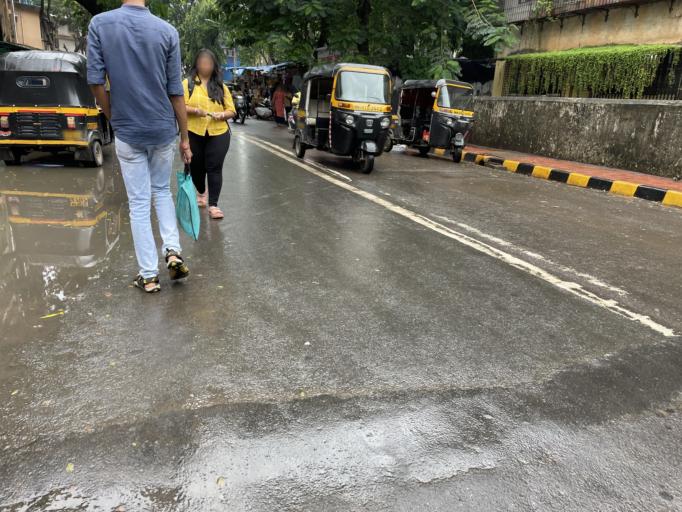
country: IN
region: Maharashtra
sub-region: Mumbai Suburban
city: Borivli
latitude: 19.2522
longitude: 72.8601
